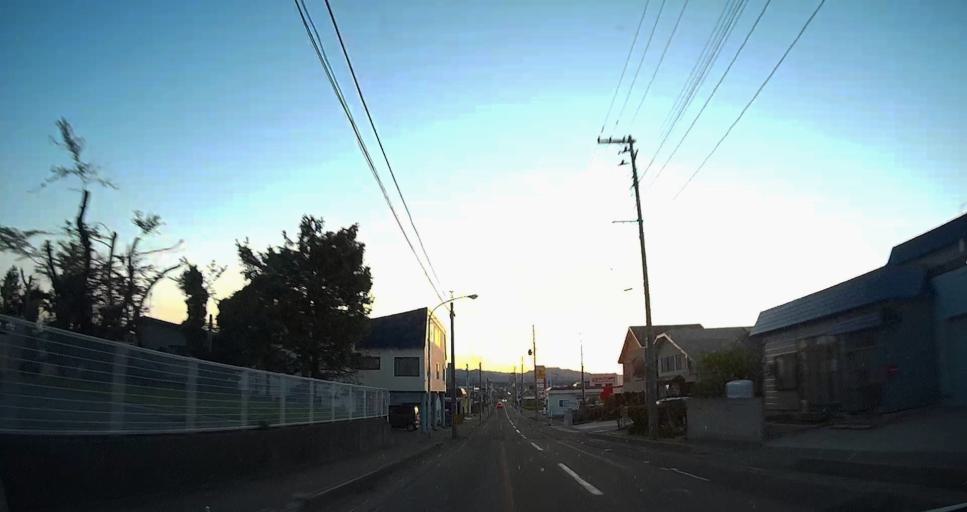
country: JP
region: Aomori
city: Misawa
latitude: 40.8687
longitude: 141.1199
